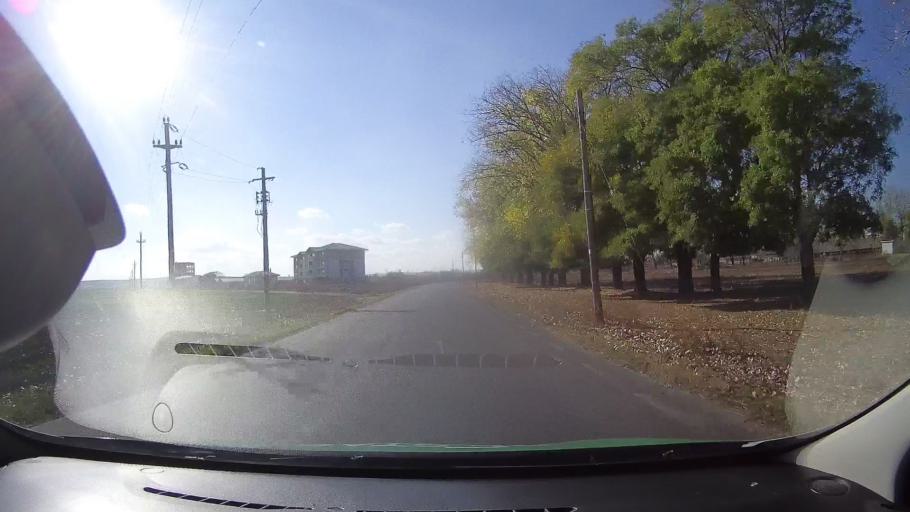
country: RO
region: Tulcea
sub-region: Comuna Baia
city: Baia
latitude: 44.7340
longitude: 28.6855
